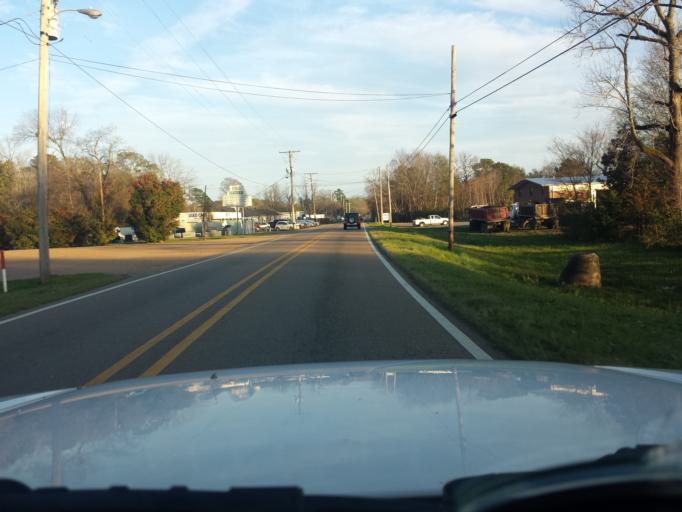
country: US
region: Mississippi
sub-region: Hinds County
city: Jackson
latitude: 32.2823
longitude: -90.1612
